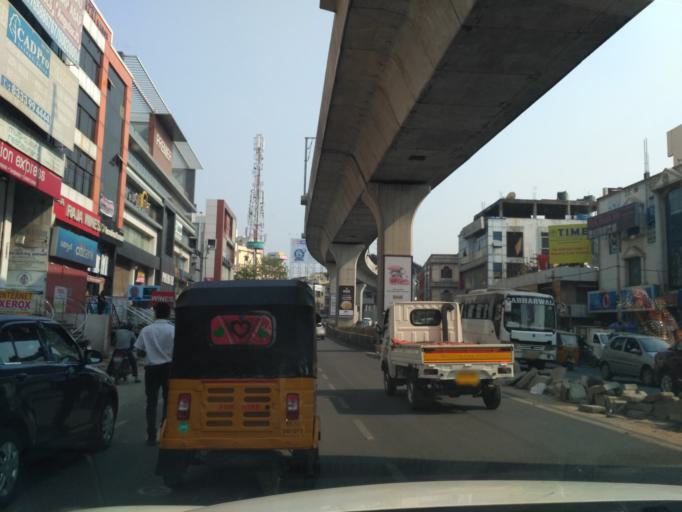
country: IN
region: Telangana
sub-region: Rangareddi
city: Kukatpalli
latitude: 17.4447
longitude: 78.3866
